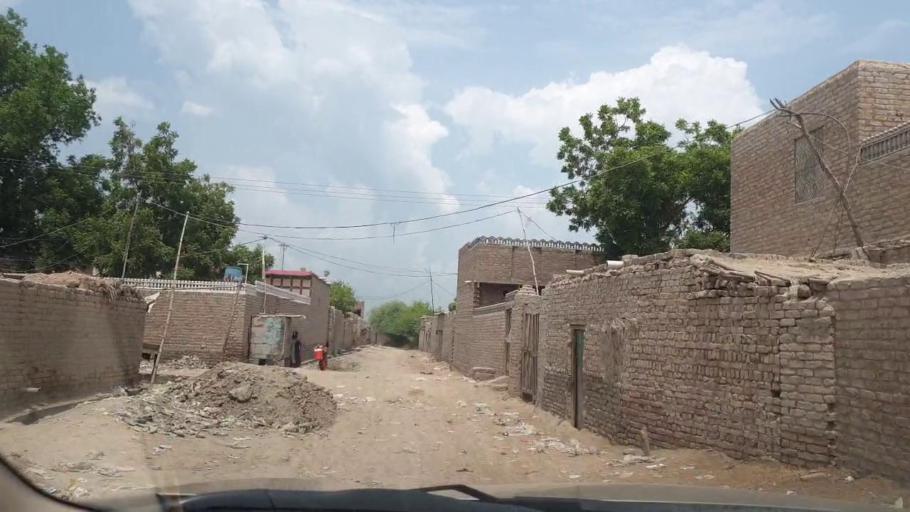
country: PK
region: Sindh
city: Larkana
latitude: 27.5669
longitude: 68.1263
